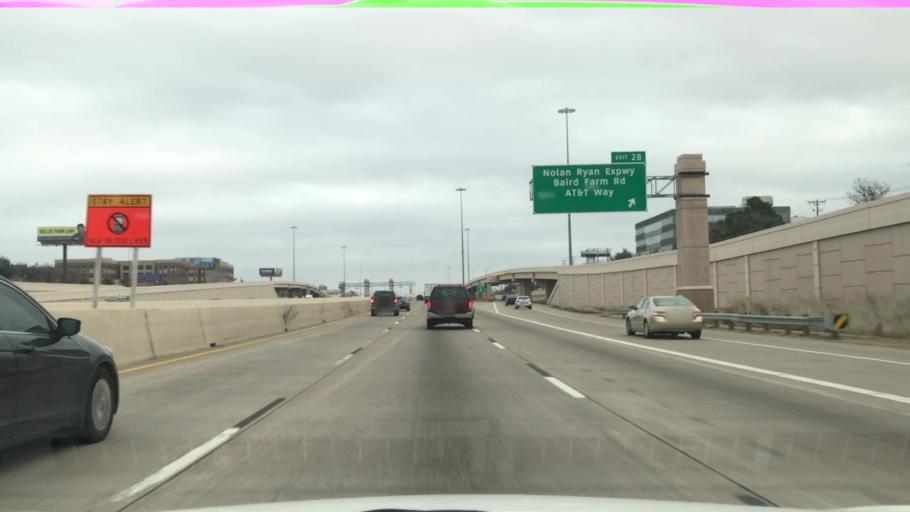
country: US
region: Texas
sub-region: Tarrant County
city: Arlington
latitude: 32.7596
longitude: -97.0962
